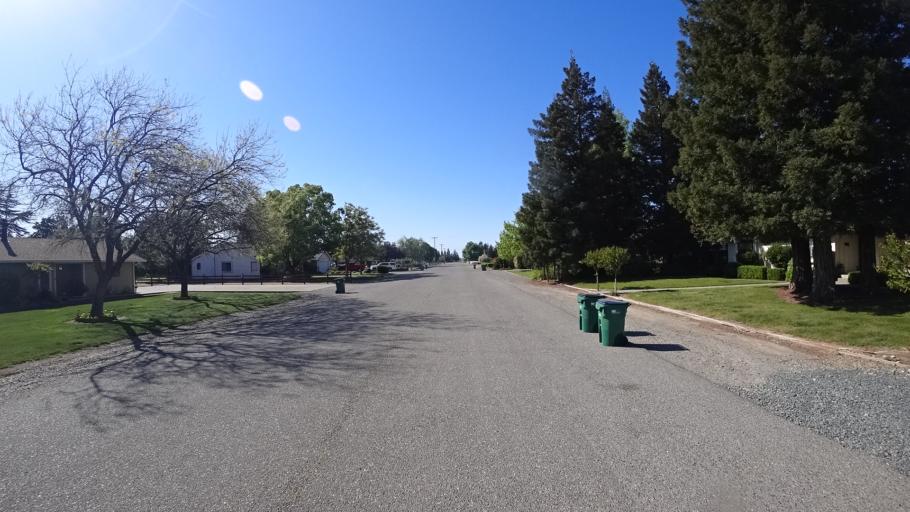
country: US
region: California
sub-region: Glenn County
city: Orland
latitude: 39.7301
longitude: -122.1654
